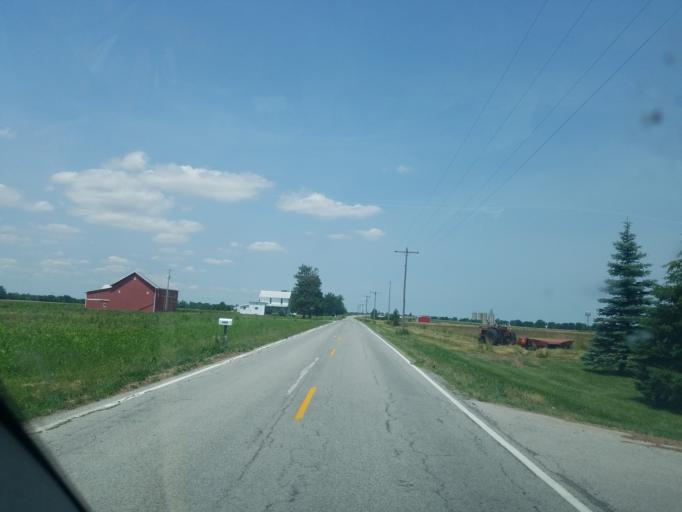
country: US
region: Ohio
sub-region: Wyandot County
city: Carey
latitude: 40.9618
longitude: -83.4860
